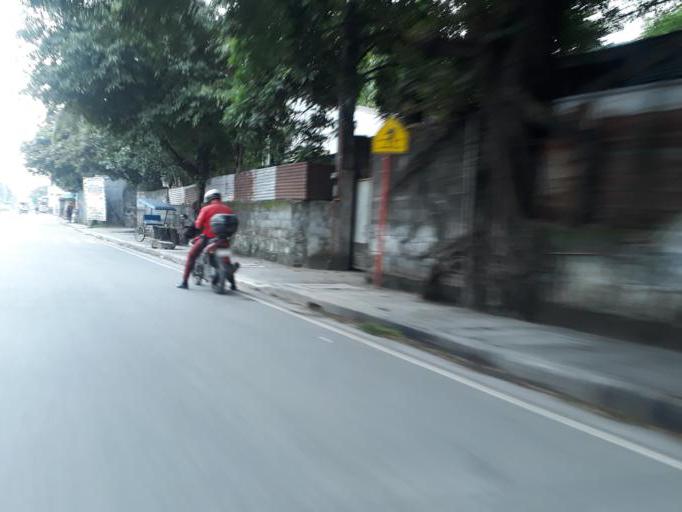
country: PH
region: Calabarzon
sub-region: Province of Rizal
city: Valenzuela
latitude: 14.6980
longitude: 120.9524
